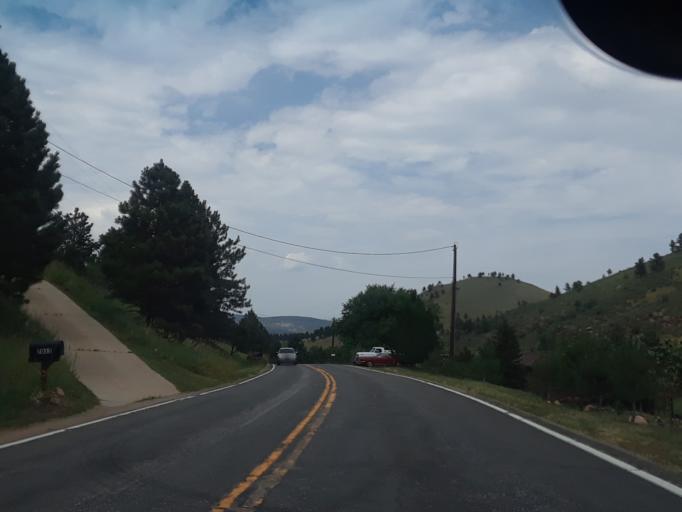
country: US
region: Colorado
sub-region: Boulder County
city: Boulder
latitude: 40.1016
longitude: -105.3023
